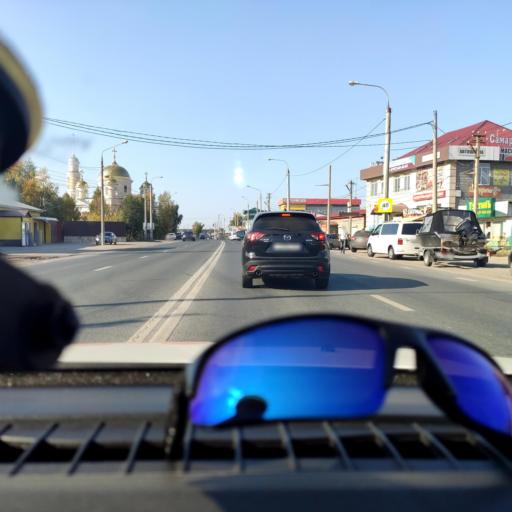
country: RU
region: Samara
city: Volzhskiy
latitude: 53.4247
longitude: 50.1239
